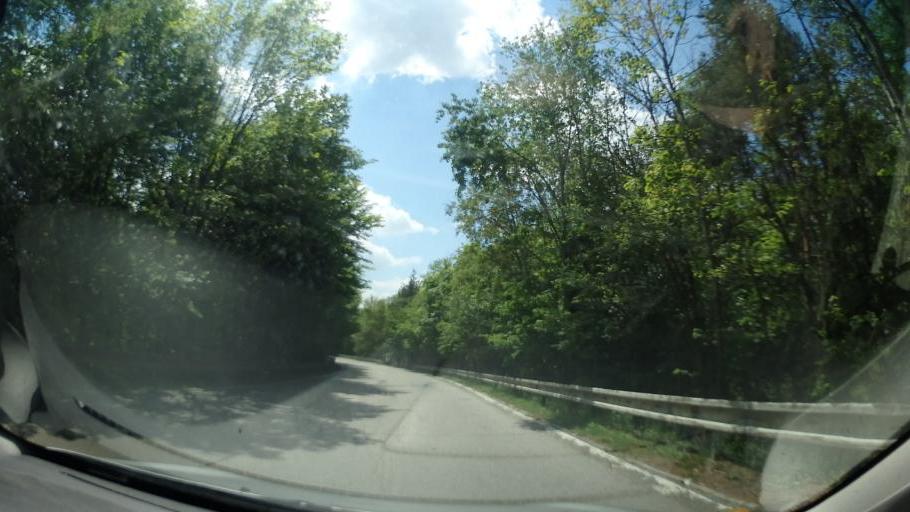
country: CZ
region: Vysocina
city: Hrotovice
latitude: 49.1684
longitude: 16.0764
